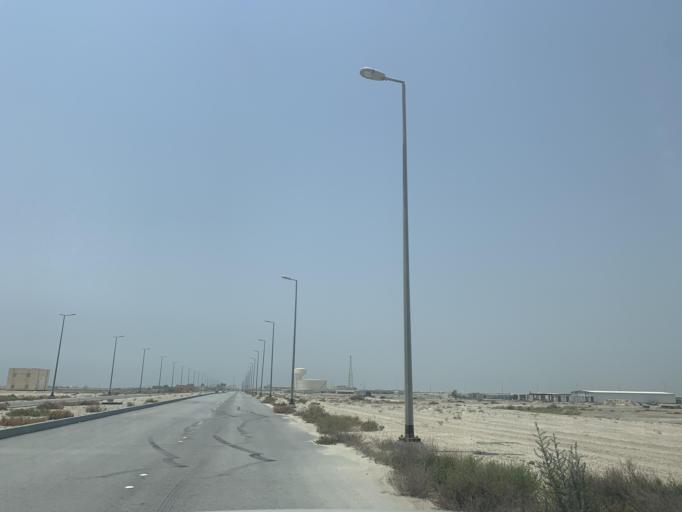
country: BH
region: Central Governorate
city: Dar Kulayb
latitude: 25.8462
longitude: 50.5906
